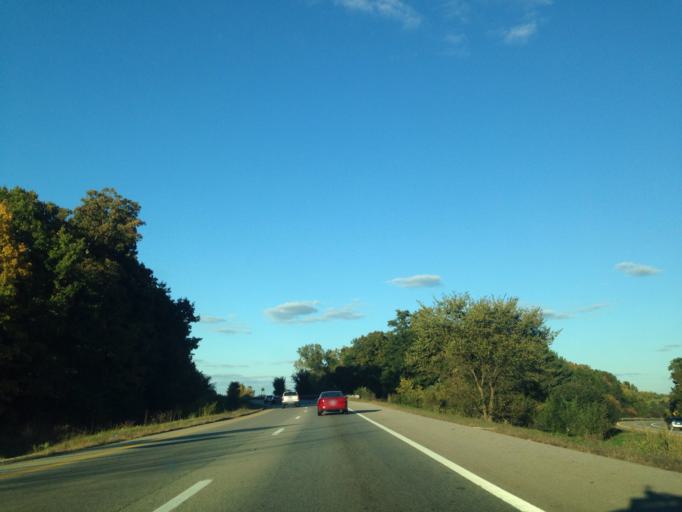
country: US
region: Michigan
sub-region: Oakland County
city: Bloomfield Hills
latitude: 42.6109
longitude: -83.2352
